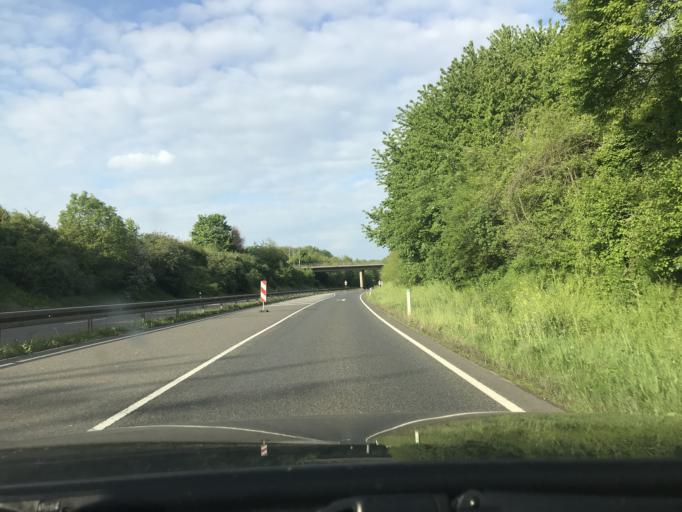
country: DE
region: North Rhine-Westphalia
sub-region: Regierungsbezirk Koln
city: Erftstadt
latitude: 50.8195
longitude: 6.8111
